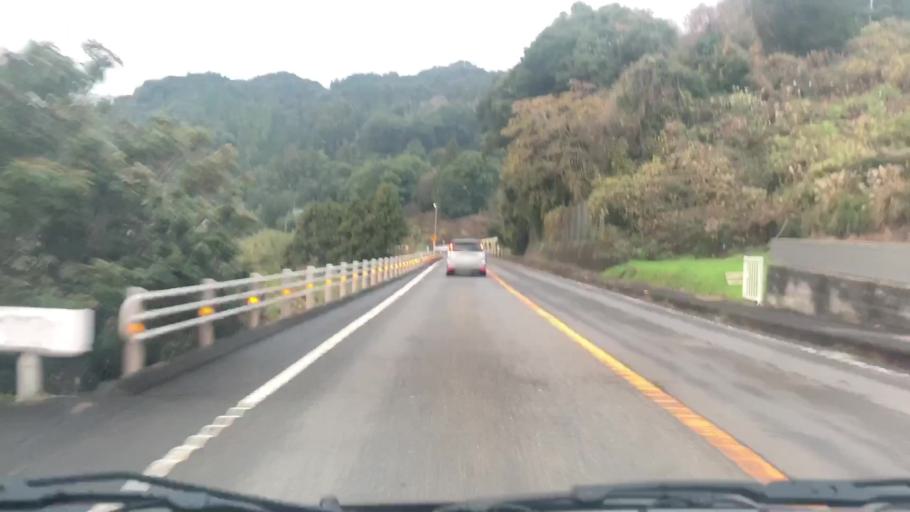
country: JP
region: Saga Prefecture
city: Ureshinomachi-shimojuku
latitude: 33.0567
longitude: 129.9475
